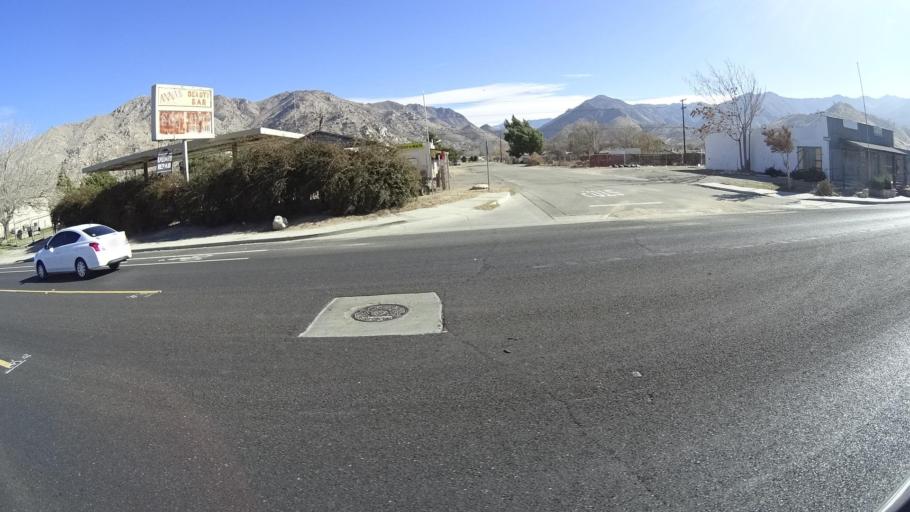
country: US
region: California
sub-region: Kern County
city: Lake Isabella
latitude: 35.6145
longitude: -118.4799
